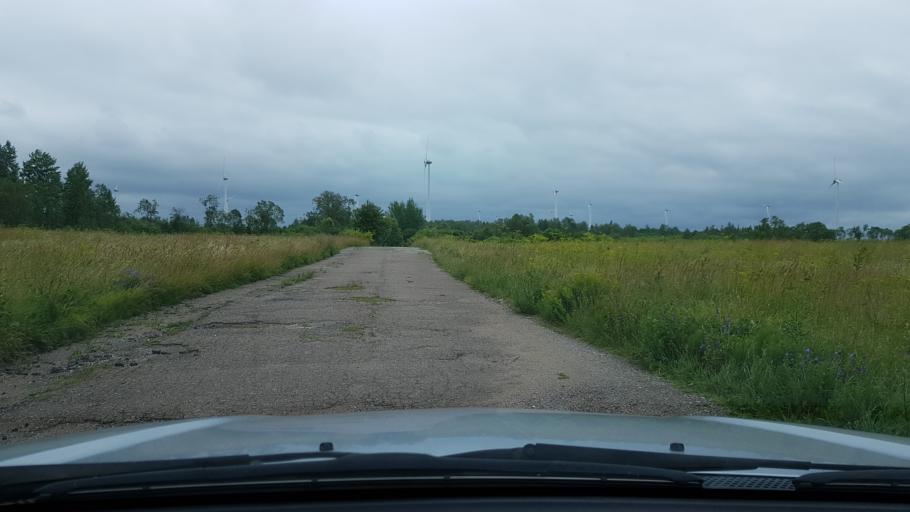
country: EE
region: Ida-Virumaa
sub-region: Narva-Joesuu linn
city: Narva-Joesuu
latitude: 59.3474
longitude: 28.0272
